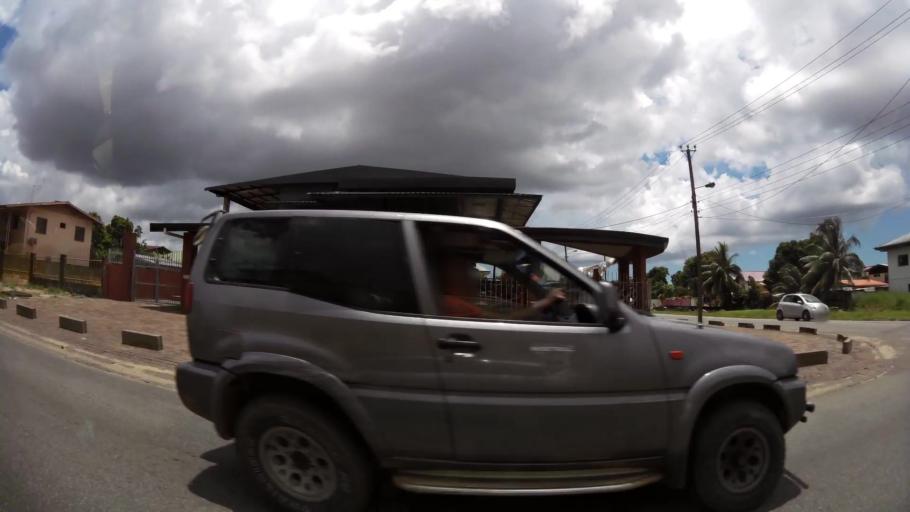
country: SR
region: Paramaribo
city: Paramaribo
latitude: 5.8538
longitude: -55.1432
